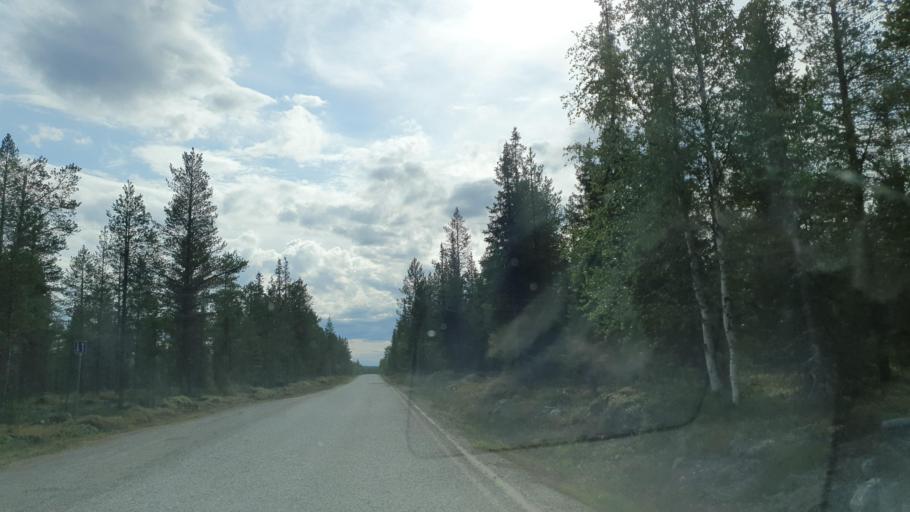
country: FI
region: Lapland
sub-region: Tunturi-Lappi
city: Muonio
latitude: 67.6979
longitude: 24.1153
